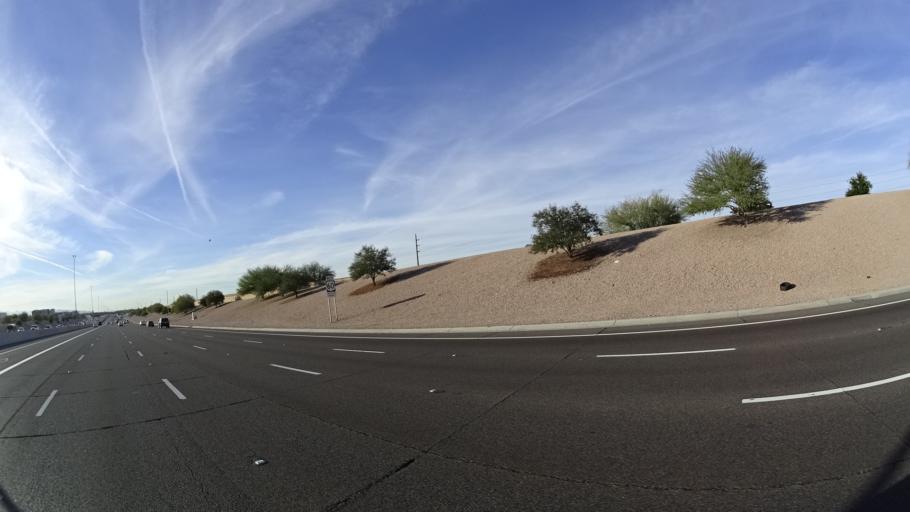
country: US
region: Arizona
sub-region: Maricopa County
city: Gilbert
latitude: 33.3863
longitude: -111.7074
